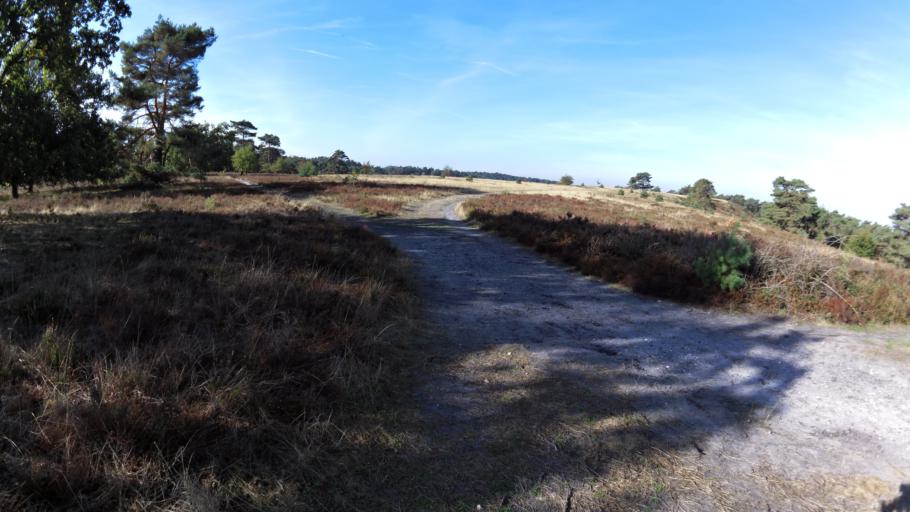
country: NL
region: Limburg
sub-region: Gemeente Brunssum
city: Brunssum
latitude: 50.9220
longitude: 6.0064
